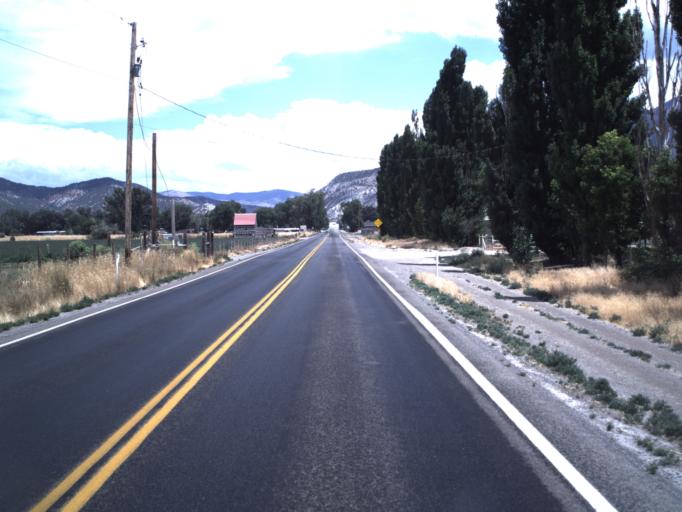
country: US
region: Utah
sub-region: Juab County
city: Nephi
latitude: 39.7100
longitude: -111.8508
